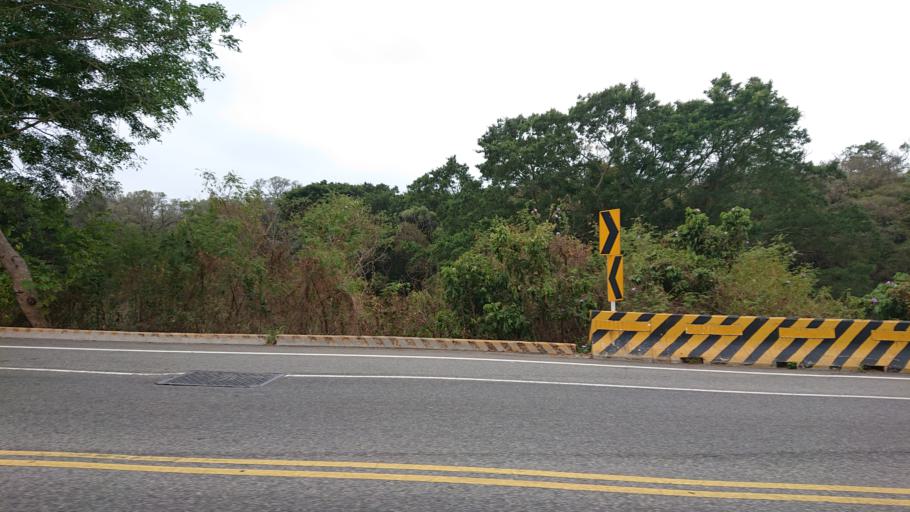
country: TW
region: Fukien
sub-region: Kinmen
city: Jincheng
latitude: 24.4396
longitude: 118.3933
